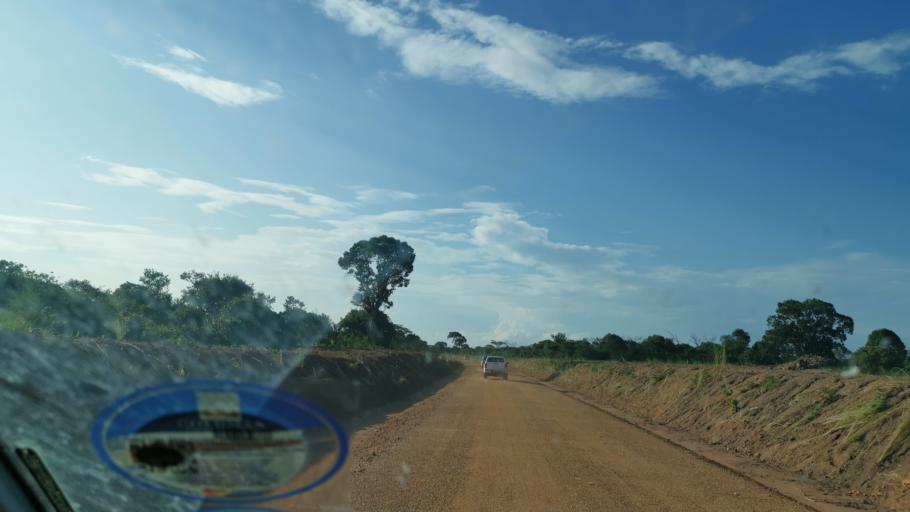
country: ZM
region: Luapula
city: Samfya
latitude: -11.1063
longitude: 29.5742
